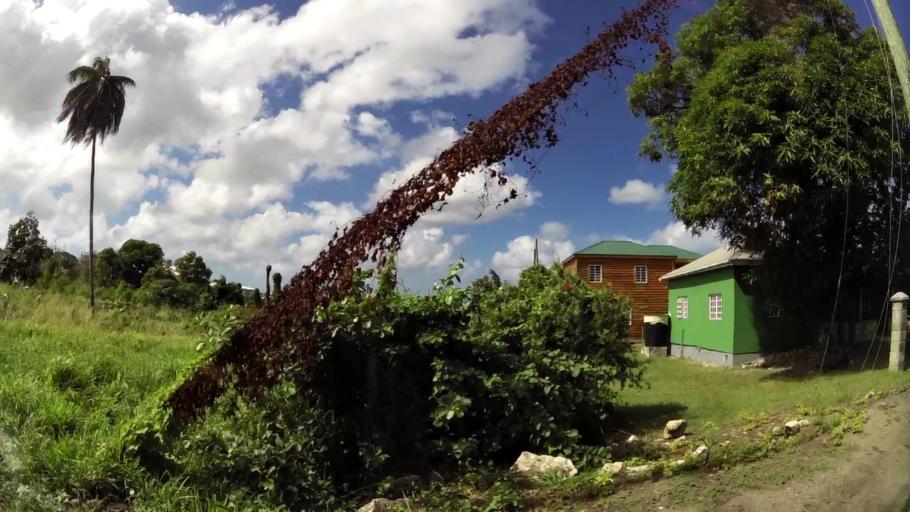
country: AG
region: Saint John
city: Saint John's
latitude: 17.1140
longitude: -61.8391
